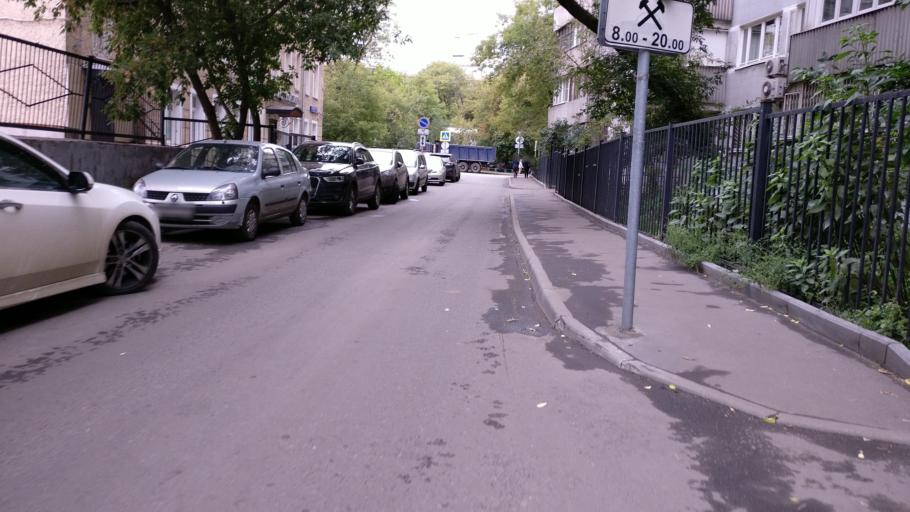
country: RU
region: Moscow
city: Sokol'niki
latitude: 55.7756
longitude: 37.6455
